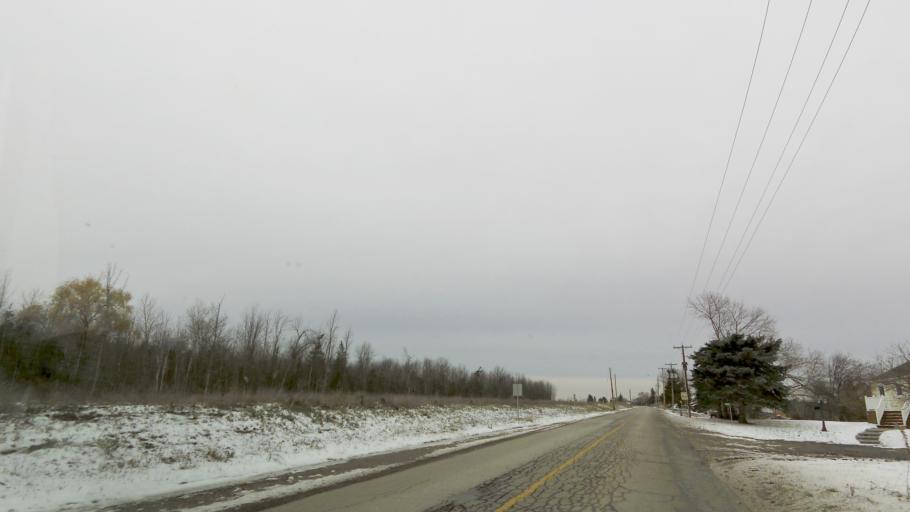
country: CA
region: Ontario
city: Bradford West Gwillimbury
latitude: 44.0588
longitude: -79.5967
